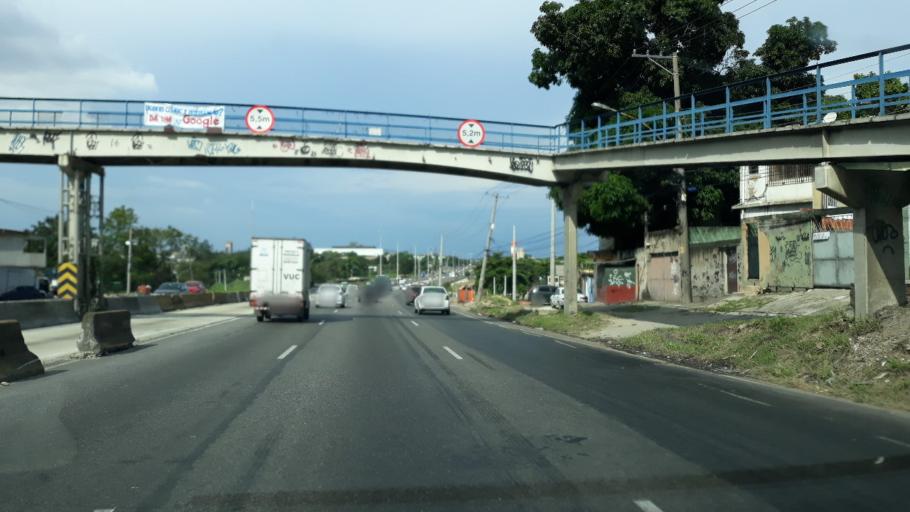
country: BR
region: Rio de Janeiro
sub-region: Sao Joao De Meriti
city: Sao Joao de Meriti
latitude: -22.8356
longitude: -43.3617
